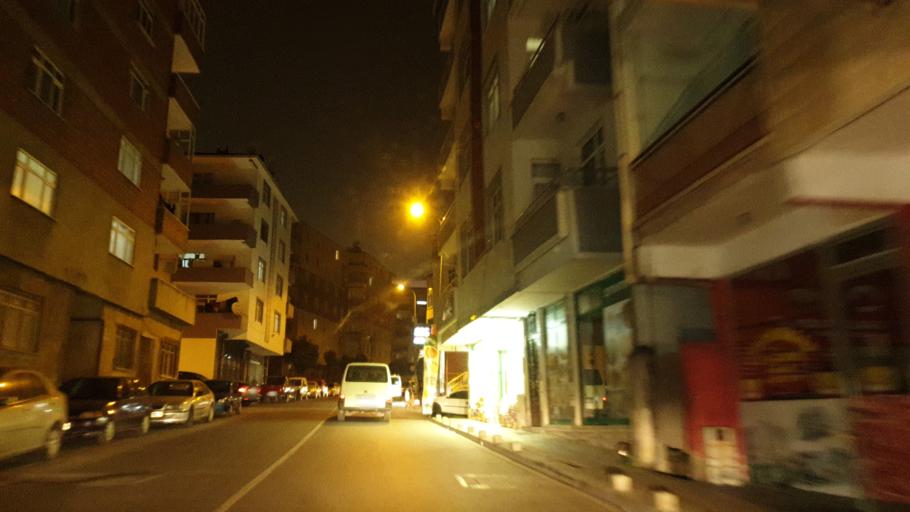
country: TR
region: Istanbul
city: Pendik
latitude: 40.8779
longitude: 29.2550
